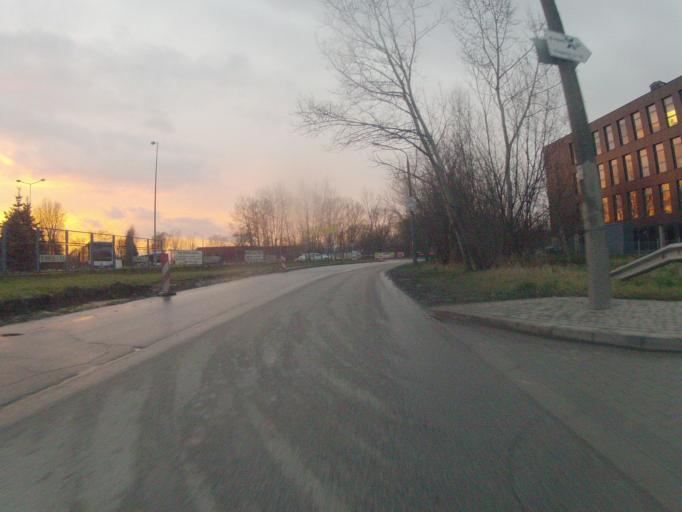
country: PL
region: Lesser Poland Voivodeship
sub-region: Powiat wielicki
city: Czarnochowice
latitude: 50.0584
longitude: 20.0245
